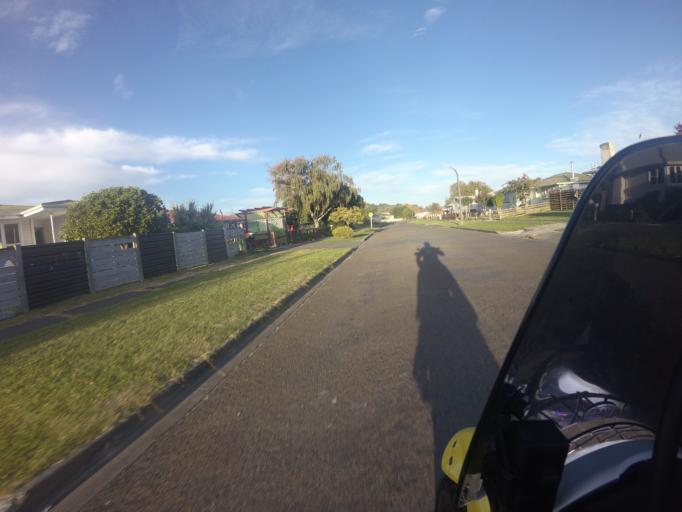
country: NZ
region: Gisborne
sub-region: Gisborne District
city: Gisborne
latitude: -38.6721
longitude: 178.0542
